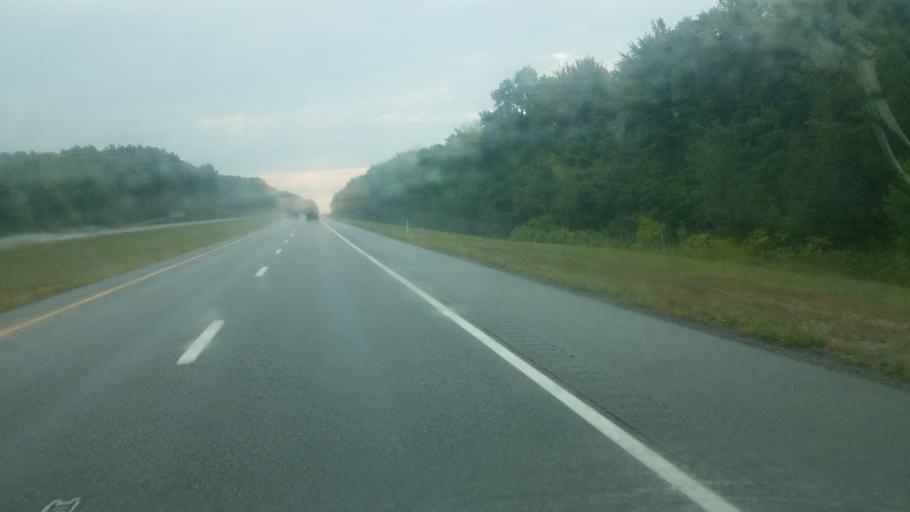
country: US
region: Ohio
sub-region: Portage County
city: Mantua
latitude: 41.3837
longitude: -81.2373
